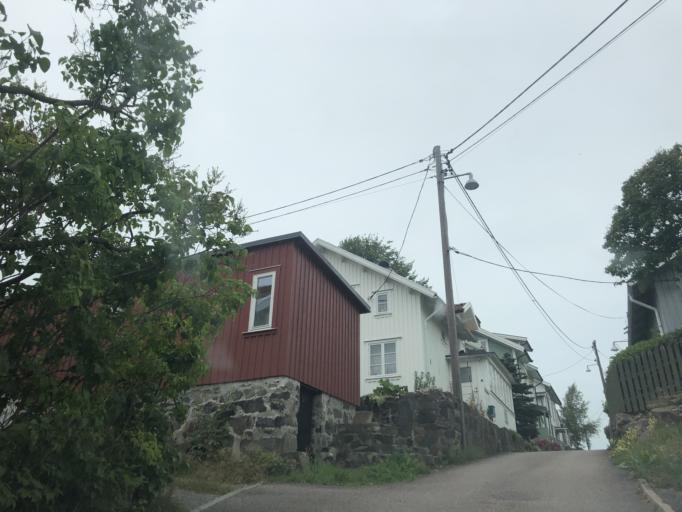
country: SE
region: Vaestra Goetaland
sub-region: Goteborg
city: Majorna
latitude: 57.7045
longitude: 11.9309
